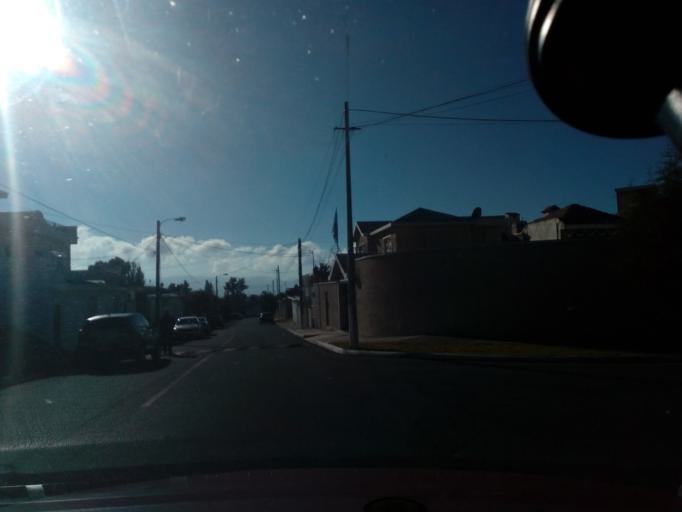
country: GT
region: Guatemala
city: Mixco
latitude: 14.6023
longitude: -90.5785
